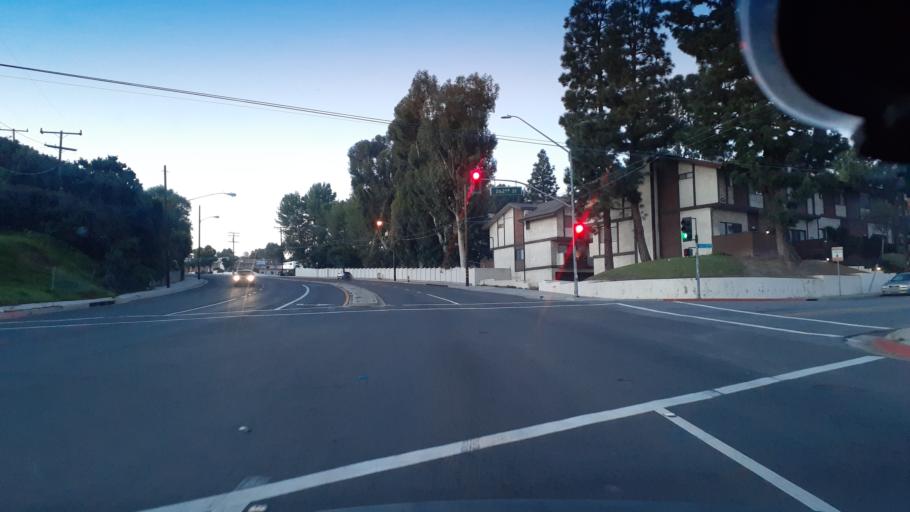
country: US
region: California
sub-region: Los Angeles County
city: Lomita
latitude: 33.7854
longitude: -118.3093
